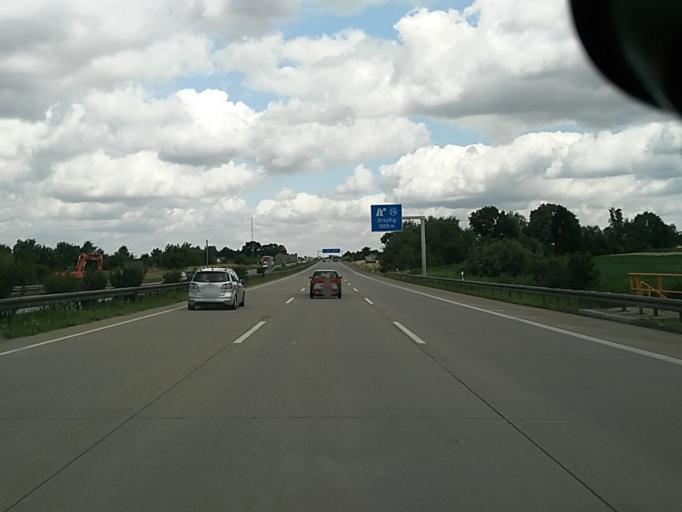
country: DE
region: Thuringia
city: Walpernhain
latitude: 51.0283
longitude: 11.9361
